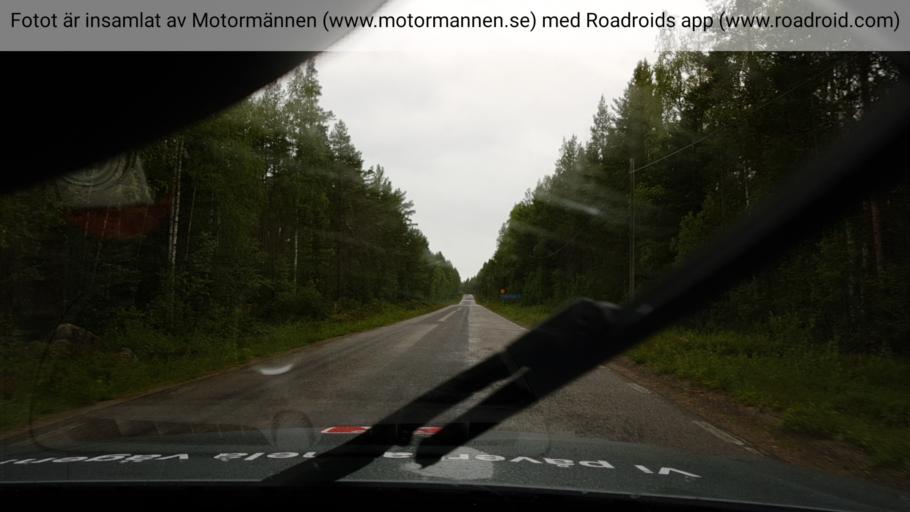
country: SE
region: Vaesternorrland
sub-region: Ange Kommun
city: Ange
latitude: 62.1770
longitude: 15.1212
